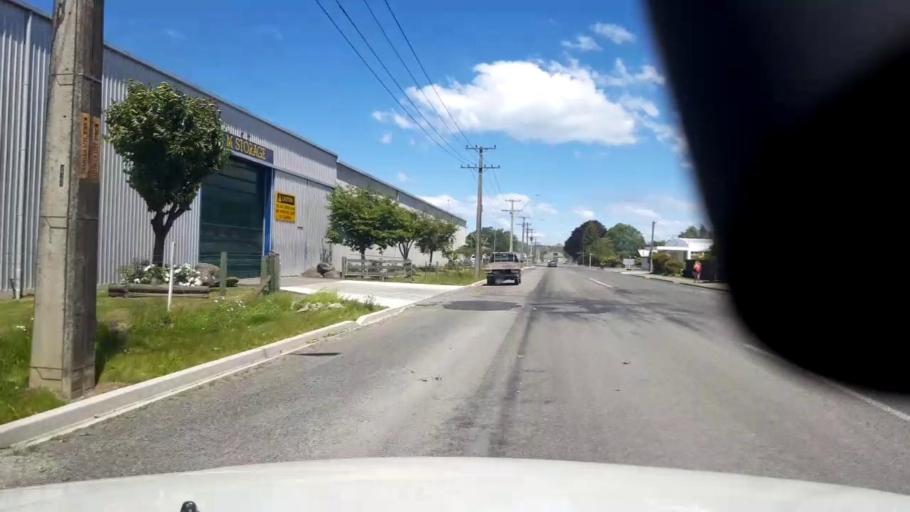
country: NZ
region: Canterbury
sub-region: Timaru District
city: Pleasant Point
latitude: -44.2396
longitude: 171.2792
